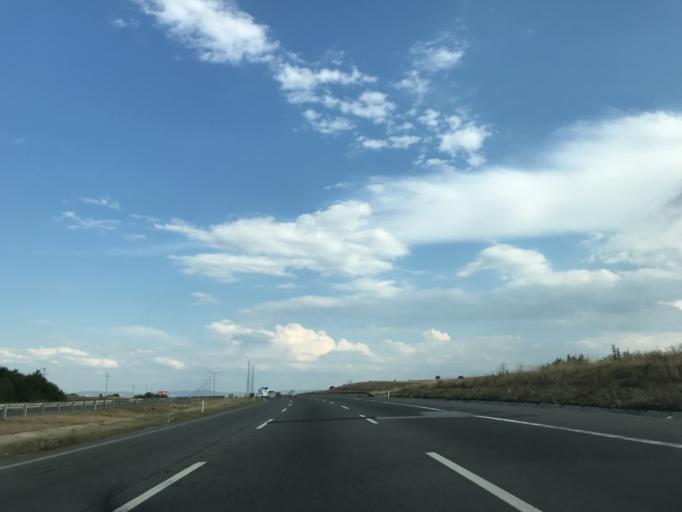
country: TR
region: Bolu
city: Yenicaga
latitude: 40.7576
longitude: 32.0645
